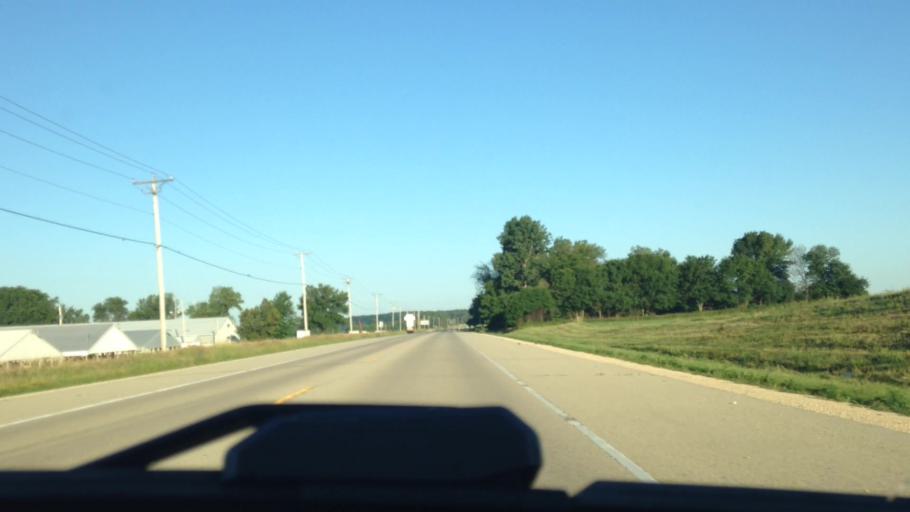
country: US
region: Wisconsin
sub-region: Dodge County
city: Juneau
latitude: 43.4445
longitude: -88.7577
